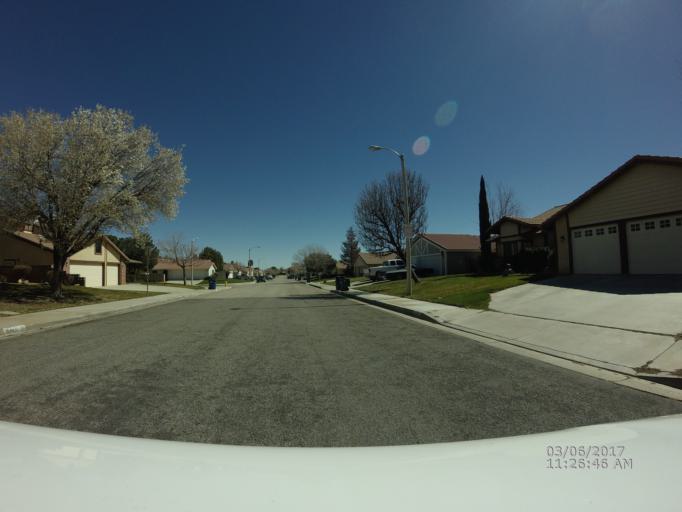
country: US
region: California
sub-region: Los Angeles County
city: Quartz Hill
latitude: 34.6502
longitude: -118.2431
